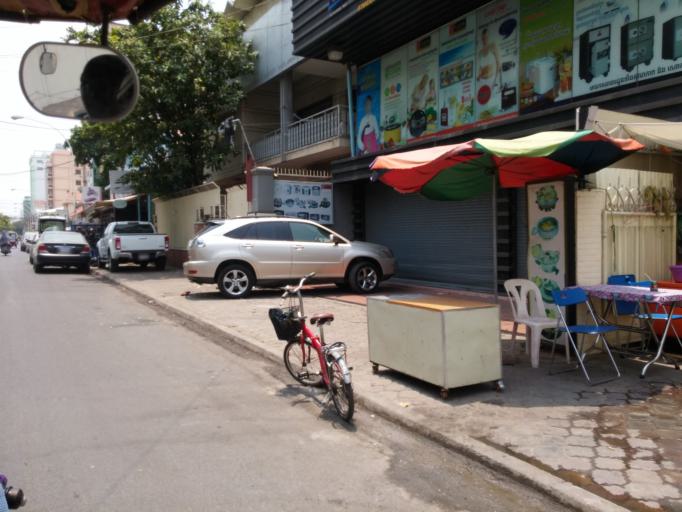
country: KH
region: Phnom Penh
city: Phnom Penh
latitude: 11.5597
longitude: 104.9190
